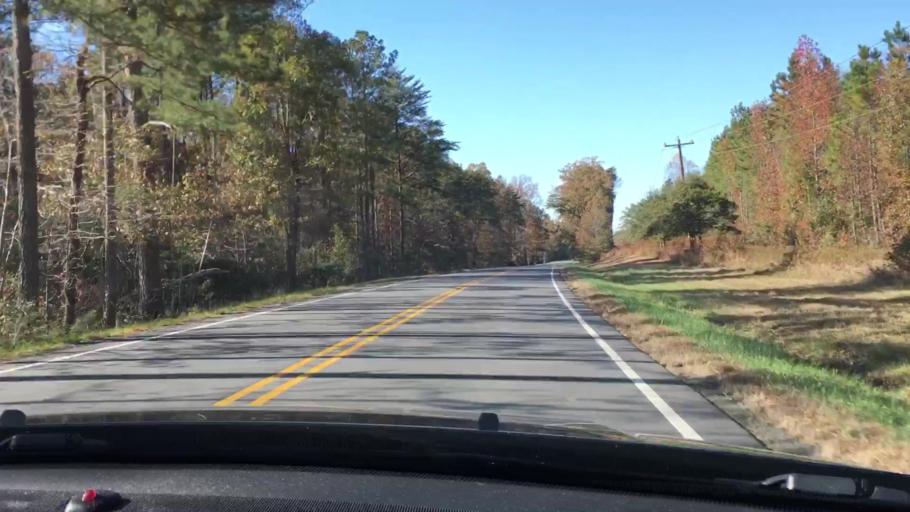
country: US
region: Virginia
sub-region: King William County
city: King William
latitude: 37.6769
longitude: -76.9985
